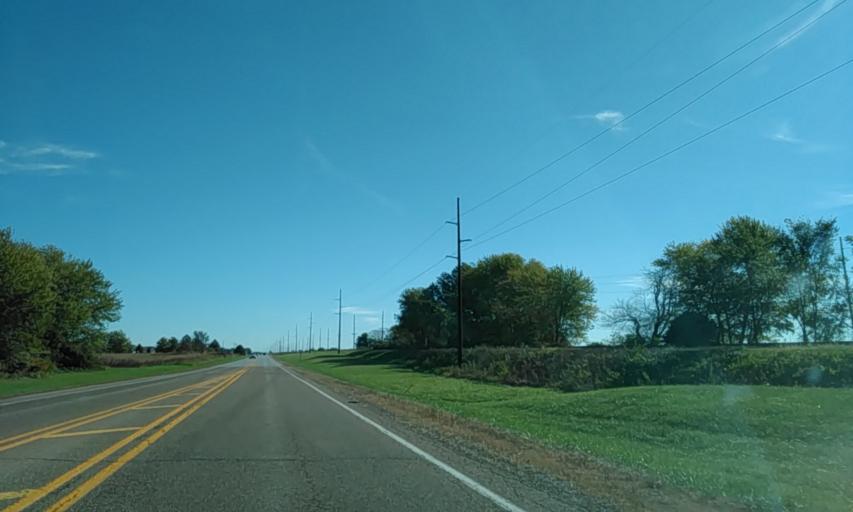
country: US
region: Illinois
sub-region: Madison County
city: Saint Jacob
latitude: 38.7209
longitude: -89.7660
